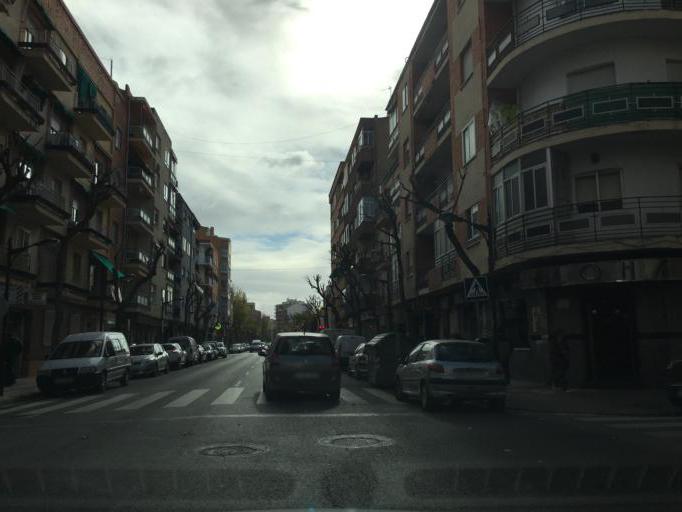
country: ES
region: Castille-La Mancha
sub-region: Provincia de Albacete
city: Albacete
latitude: 38.9949
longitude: -1.8673
